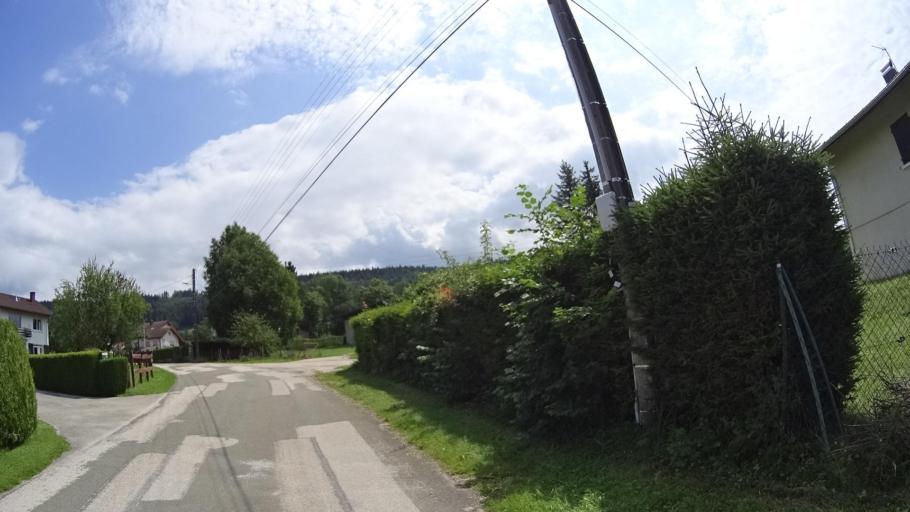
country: FR
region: Franche-Comte
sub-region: Departement du Doubs
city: Les Fourgs
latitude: 46.8156
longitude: 6.3221
